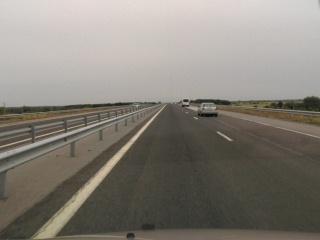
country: BG
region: Stara Zagora
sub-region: Obshtina Stara Zagora
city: Stara Zagora
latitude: 42.3216
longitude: 25.5784
